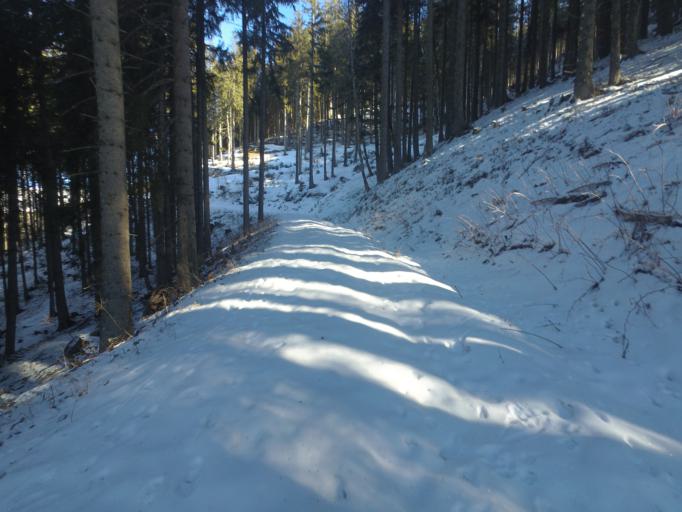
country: AT
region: Salzburg
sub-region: Politischer Bezirk Zell am See
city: Lend
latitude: 47.3276
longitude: 13.0424
